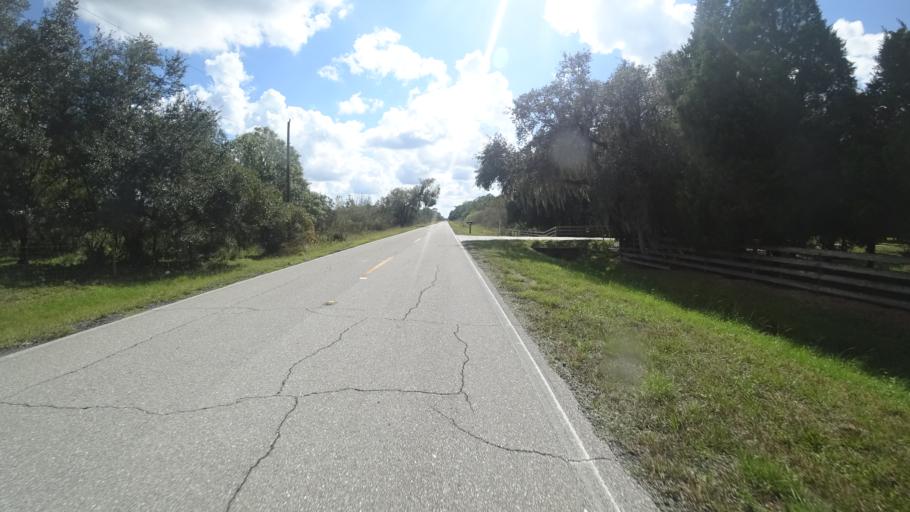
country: US
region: Florida
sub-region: Sarasota County
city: Warm Mineral Springs
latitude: 27.2555
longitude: -82.1218
